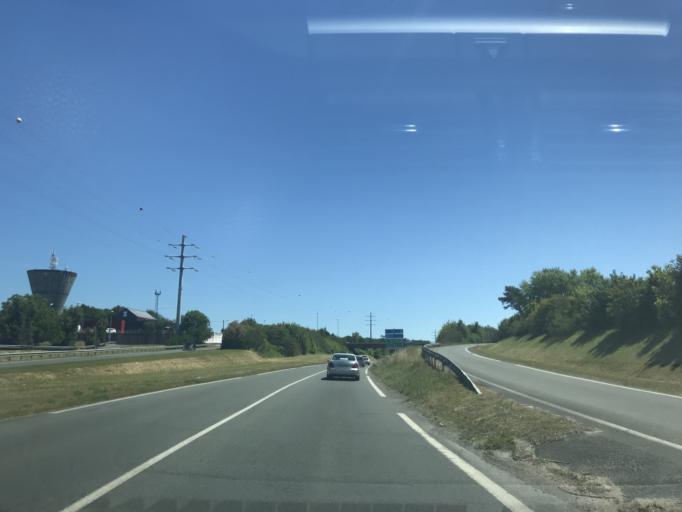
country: FR
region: Poitou-Charentes
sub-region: Departement de la Charente-Maritime
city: Saint-Georges-de-Didonne
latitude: 45.6278
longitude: -1.0013
